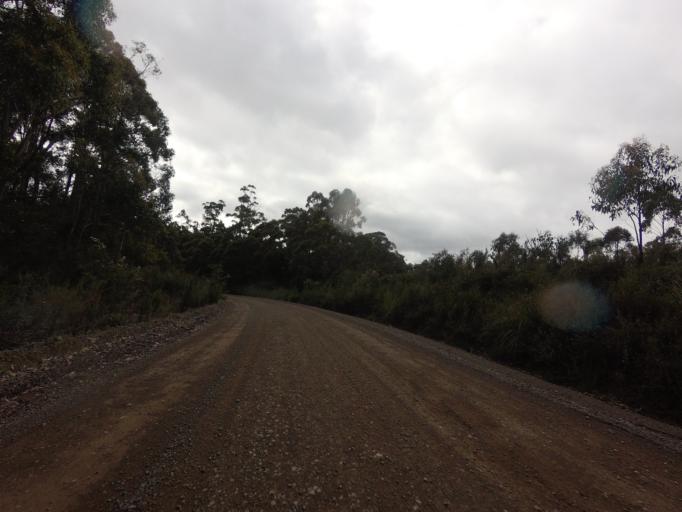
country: AU
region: Tasmania
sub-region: Huon Valley
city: Geeveston
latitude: -43.4674
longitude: 146.8989
